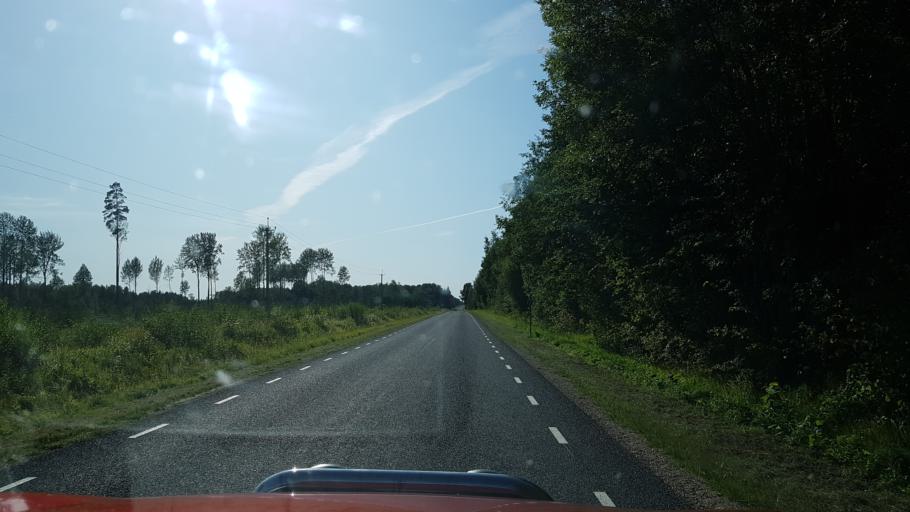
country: LV
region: Aloja
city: Staicele
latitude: 58.0900
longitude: 24.6439
